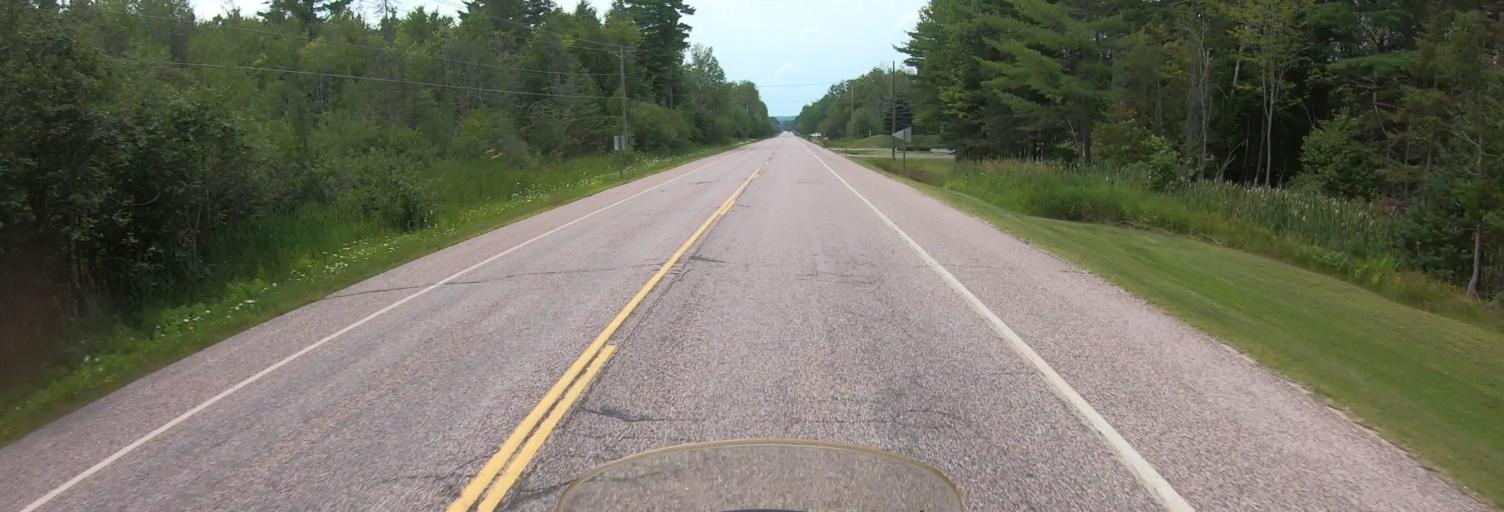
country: US
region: Michigan
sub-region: Marquette County
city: Harvey
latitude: 46.4635
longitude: -87.3281
